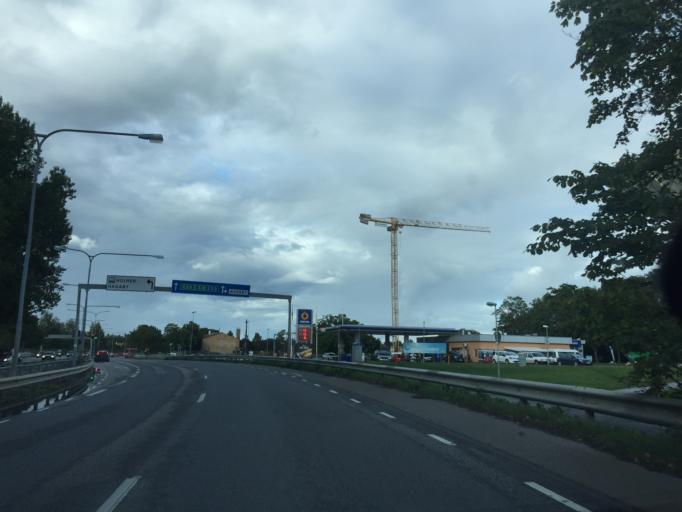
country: SE
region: OErebro
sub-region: Orebro Kommun
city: Orebro
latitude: 59.2874
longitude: 15.2227
